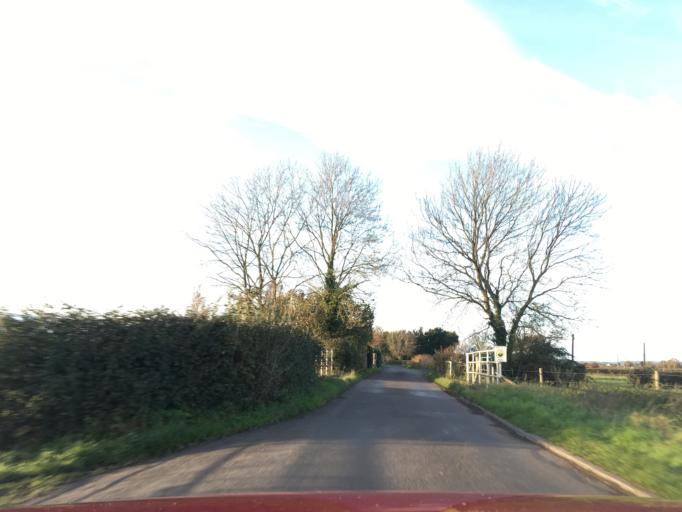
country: GB
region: England
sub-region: South Gloucestershire
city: Hill
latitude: 51.6444
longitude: -2.5103
